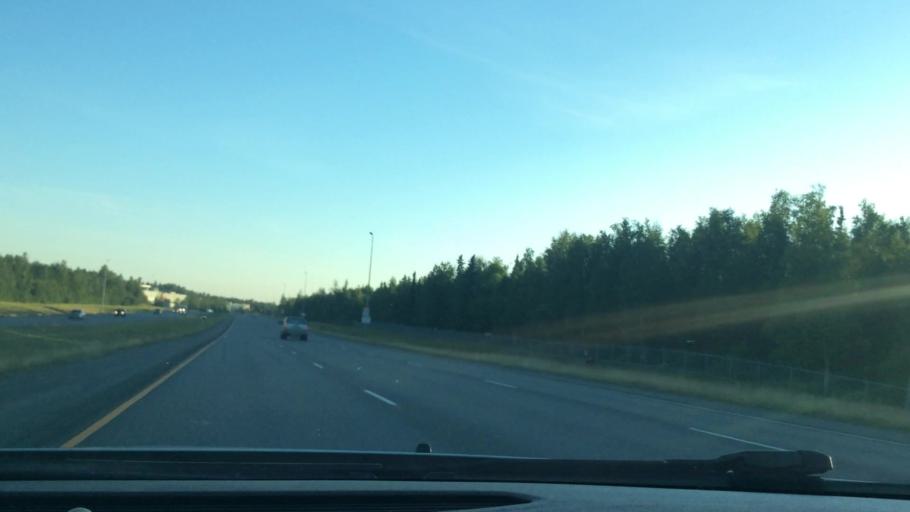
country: US
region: Alaska
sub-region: Anchorage Municipality
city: Elmendorf Air Force Base
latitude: 61.2363
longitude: -149.6999
